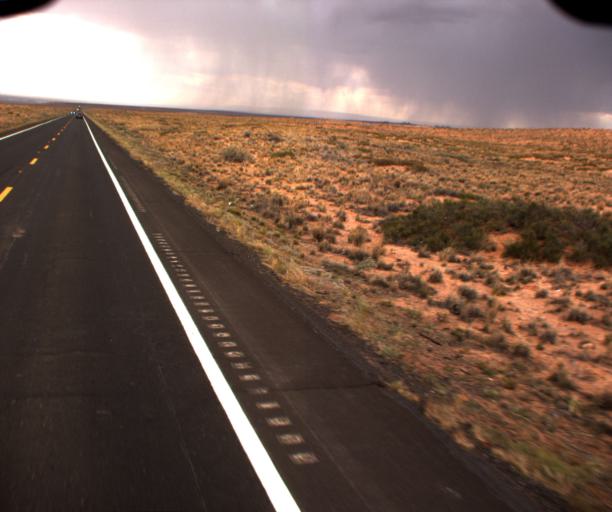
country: US
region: Arizona
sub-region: Coconino County
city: Tuba City
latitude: 36.2181
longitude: -111.0431
